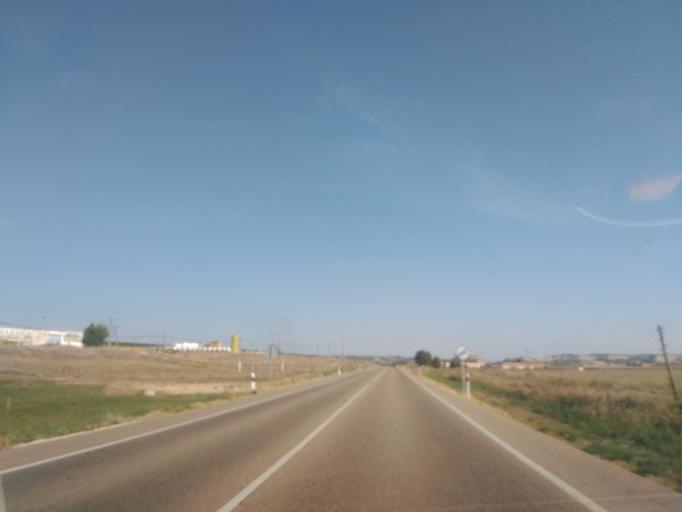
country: ES
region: Castille and Leon
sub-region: Provincia de Valladolid
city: Manzanillo
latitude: 41.6103
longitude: -4.1620
